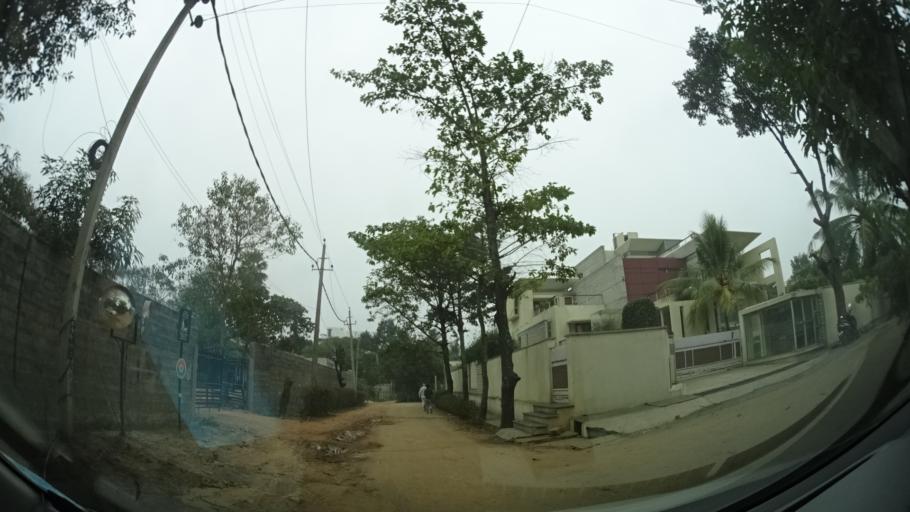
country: IN
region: Karnataka
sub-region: Bangalore Rural
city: Hoskote
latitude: 12.9703
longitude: 77.7451
